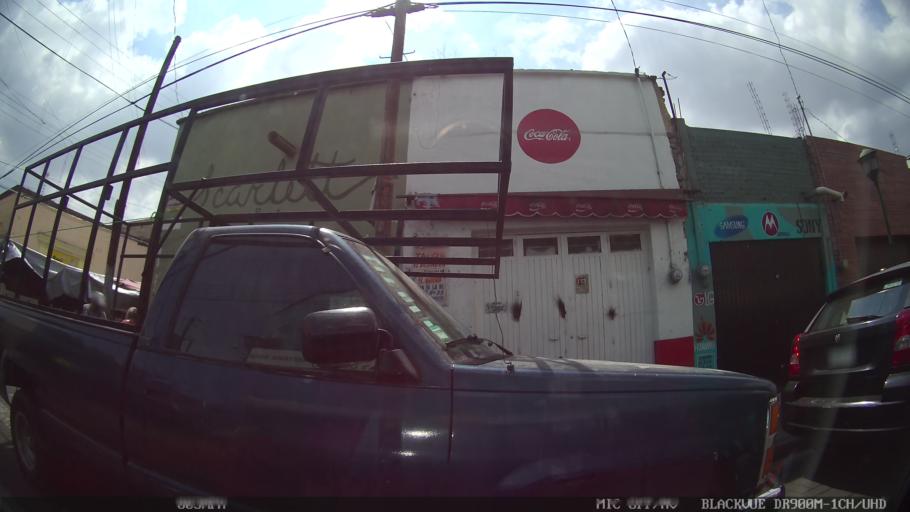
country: MX
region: Jalisco
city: Tonala
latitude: 20.6245
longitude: -103.2440
